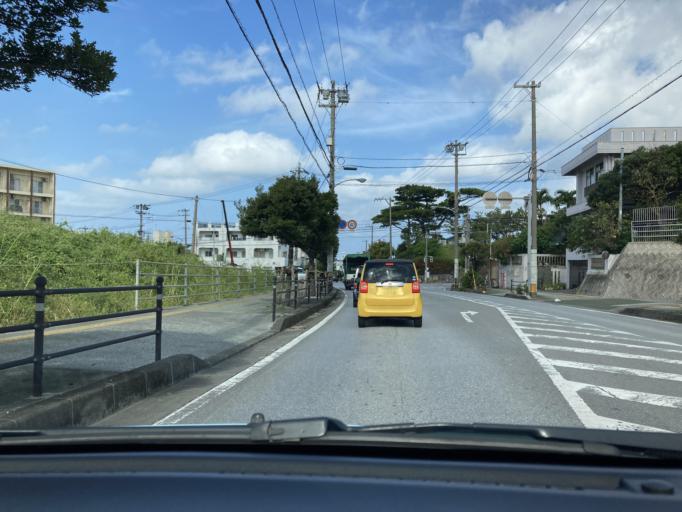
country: JP
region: Okinawa
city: Ginowan
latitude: 26.2631
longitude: 127.7492
